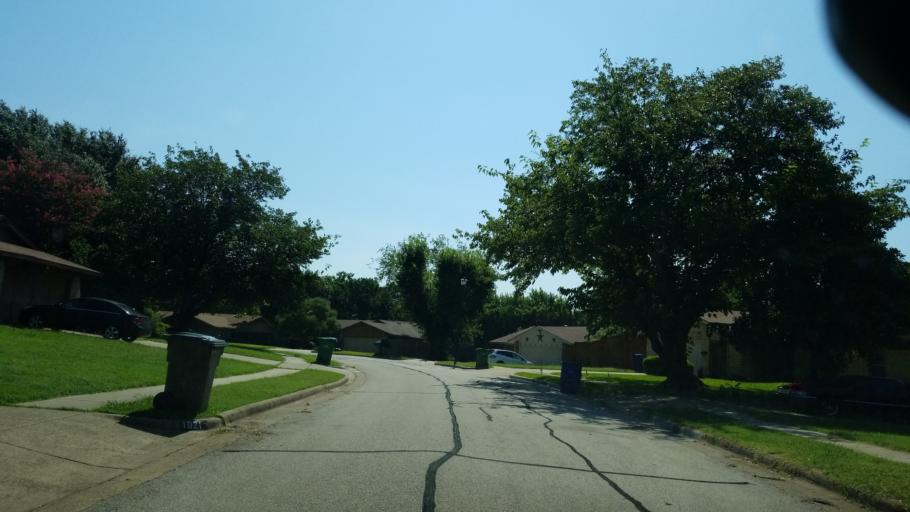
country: US
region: Texas
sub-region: Dallas County
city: Carrollton
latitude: 32.9632
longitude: -96.9042
